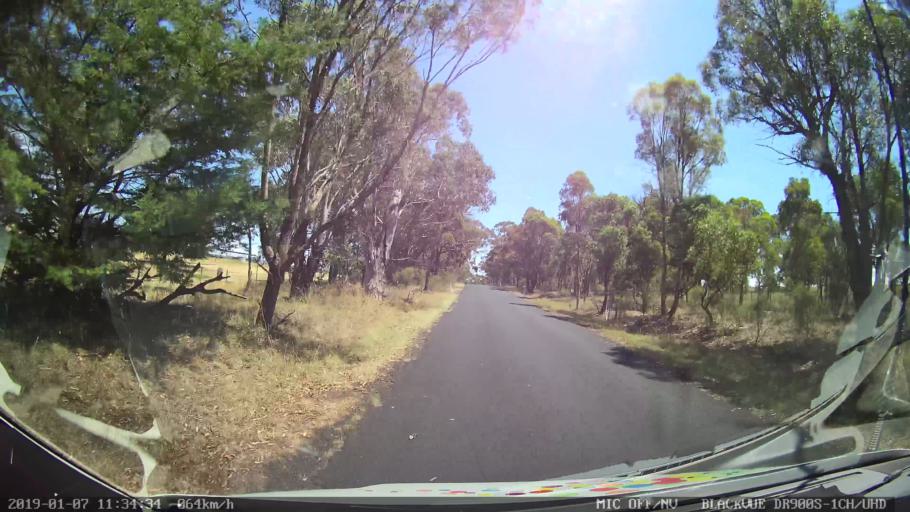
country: AU
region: New South Wales
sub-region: Armidale Dumaresq
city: Armidale
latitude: -30.3887
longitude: 151.5583
